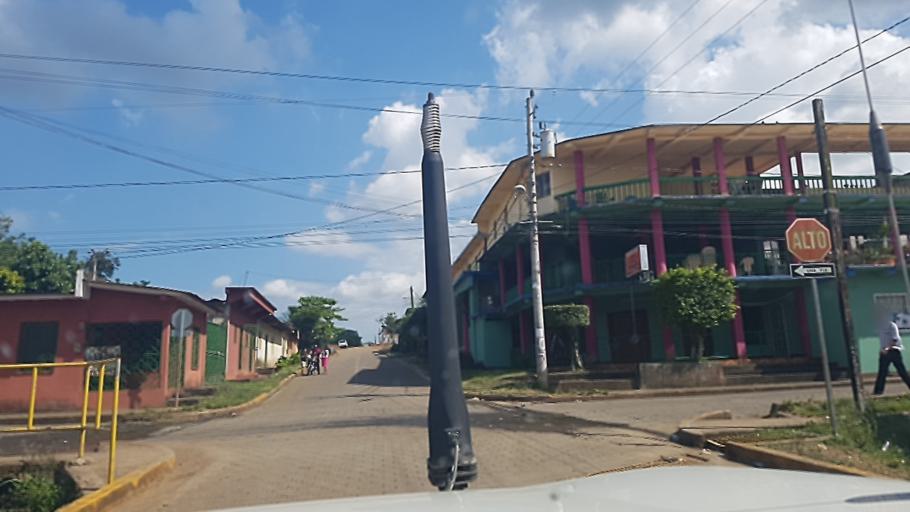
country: NI
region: Atlantico Sur
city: Nueva Guinea
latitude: 11.6878
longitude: -84.4601
